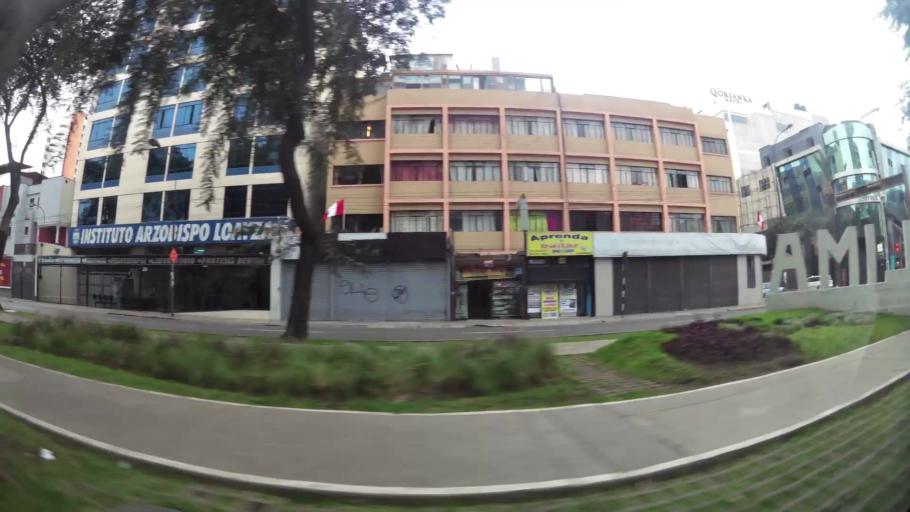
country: PE
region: Lima
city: Lima
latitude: -12.0795
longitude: -77.0352
